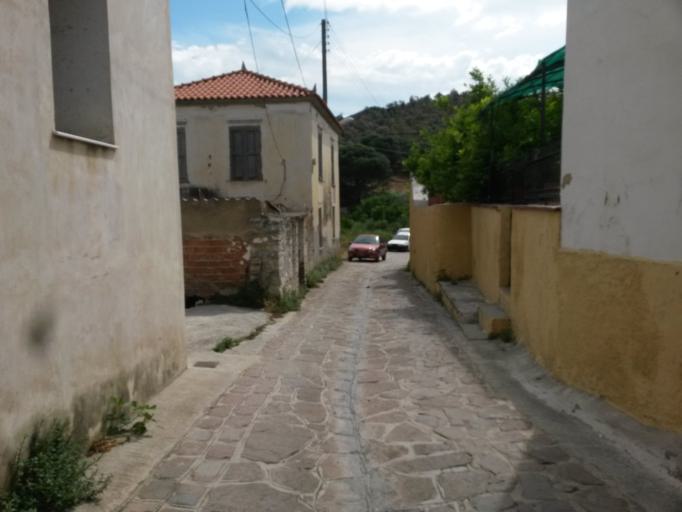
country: GR
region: North Aegean
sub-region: Nomos Lesvou
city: Moria
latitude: 39.1306
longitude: 26.5164
